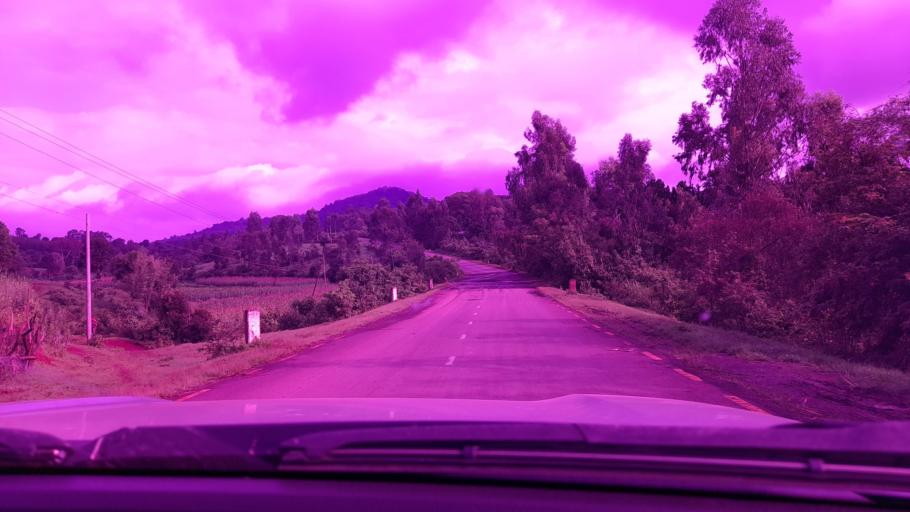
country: ET
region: Oromiya
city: Bedele
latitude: 8.2323
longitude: 36.4506
